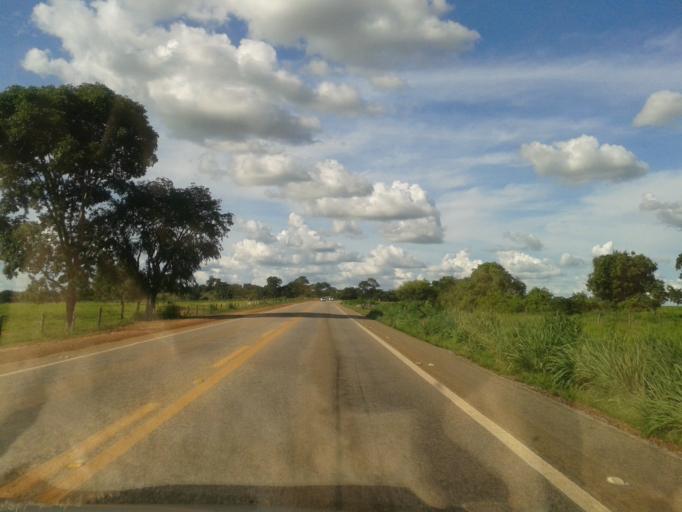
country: BR
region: Goias
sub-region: Mozarlandia
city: Mozarlandia
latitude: -14.7014
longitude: -50.5460
